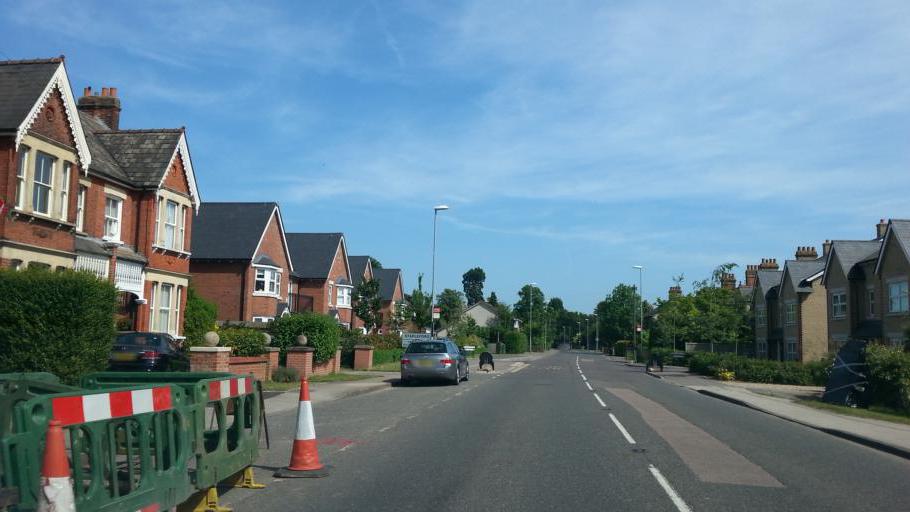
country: GB
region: England
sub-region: Cambridgeshire
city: Sawston
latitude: 52.1459
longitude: 0.1415
